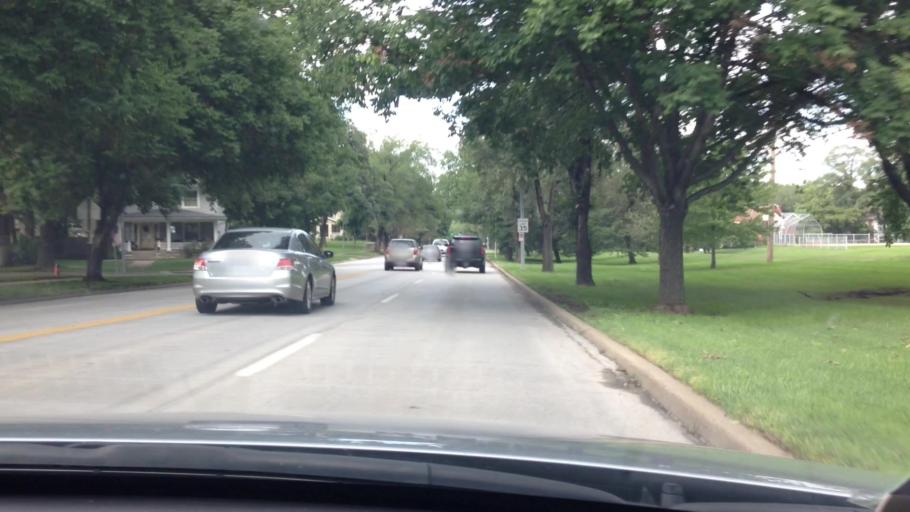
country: US
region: Kansas
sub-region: Johnson County
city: Mission Hills
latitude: 39.0244
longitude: -94.5861
